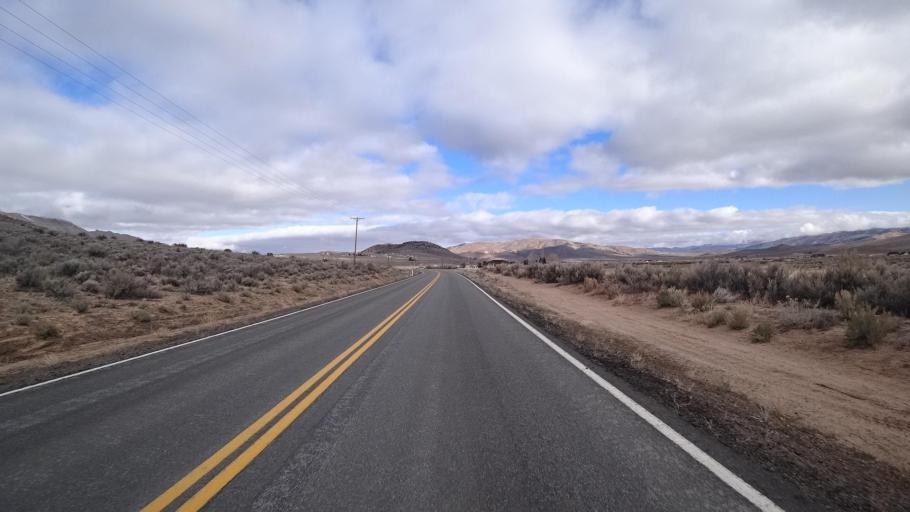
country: US
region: Nevada
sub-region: Washoe County
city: Cold Springs
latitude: 39.8591
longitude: -119.9357
